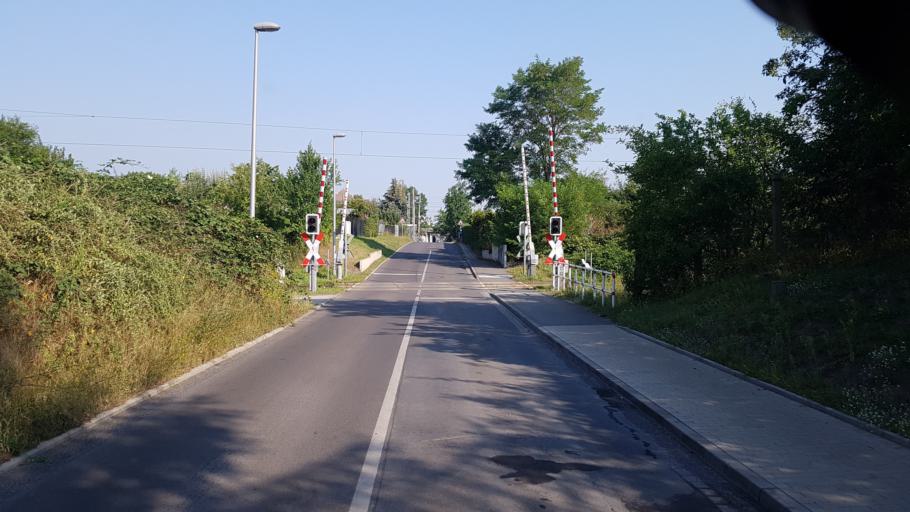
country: DE
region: Brandenburg
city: Cottbus
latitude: 51.7485
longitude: 14.3065
